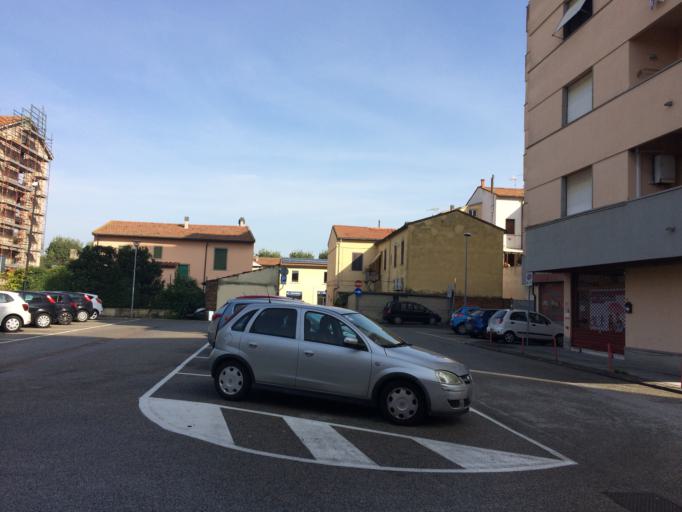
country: IT
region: Tuscany
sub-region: Province of Pisa
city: Pontedera
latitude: 43.6642
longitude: 10.6271
